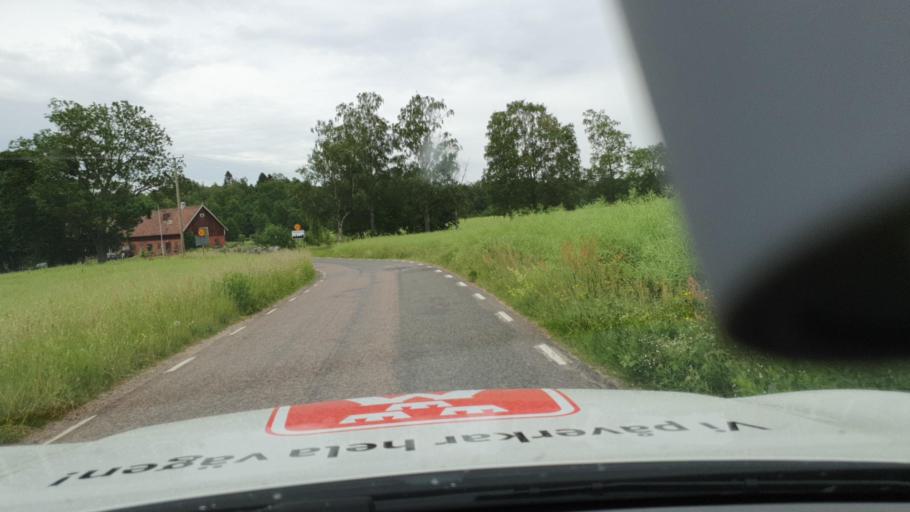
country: SE
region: Vaestra Goetaland
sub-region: Hjo Kommun
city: Hjo
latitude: 58.3066
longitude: 14.2463
